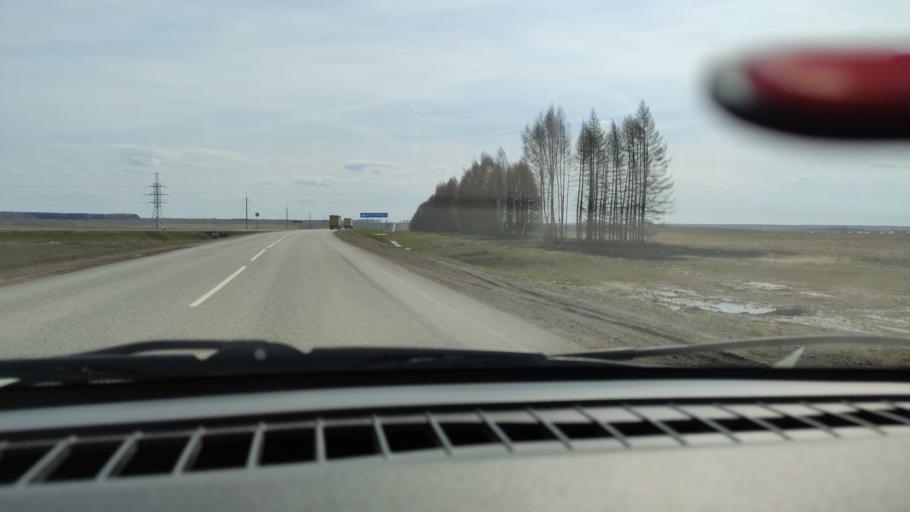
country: RU
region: Bashkortostan
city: Dyurtyuli
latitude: 55.3342
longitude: 54.9552
